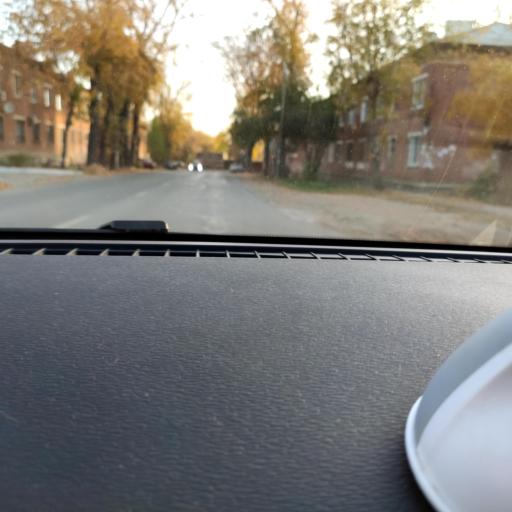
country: RU
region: Samara
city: Samara
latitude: 53.2316
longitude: 50.2392
